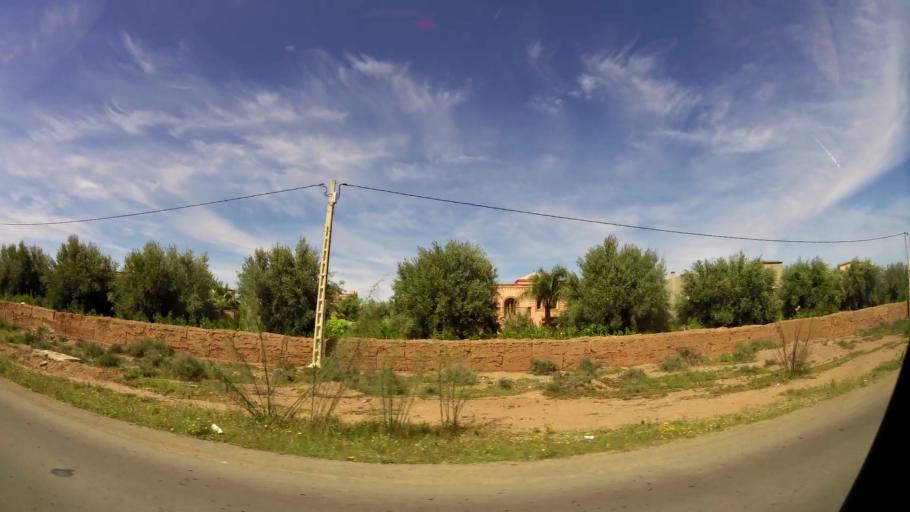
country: MA
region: Marrakech-Tensift-Al Haouz
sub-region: Marrakech
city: Marrakesh
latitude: 31.6111
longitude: -7.9412
